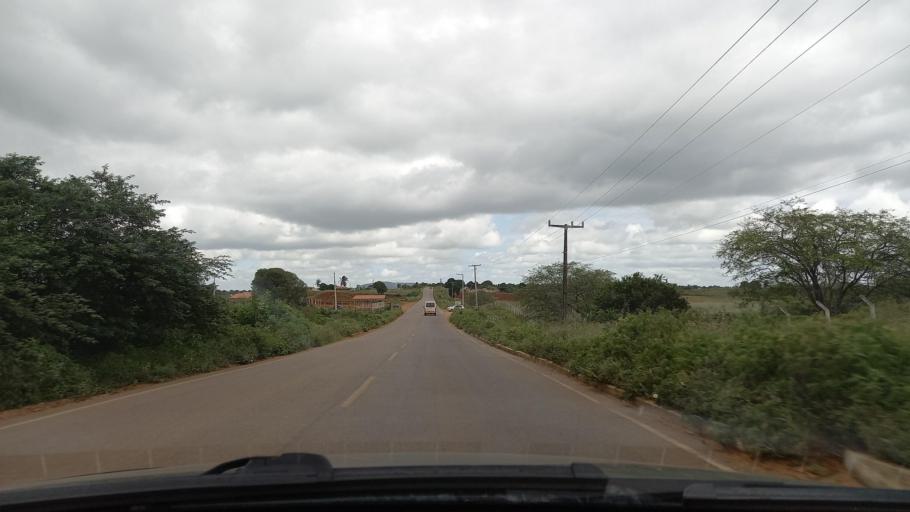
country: BR
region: Sergipe
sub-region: Caninde De Sao Francisco
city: Caninde de Sao Francisco
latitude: -9.6724
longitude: -37.7999
